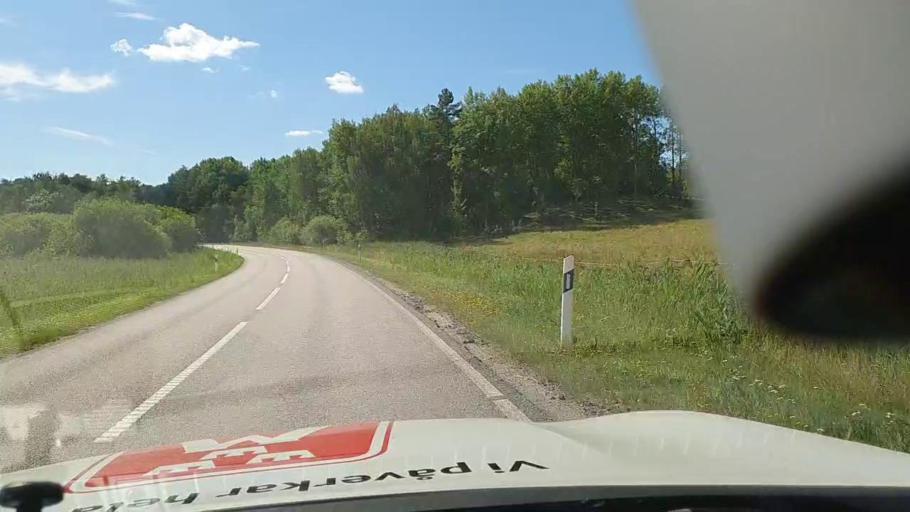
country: SE
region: Soedermanland
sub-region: Strangnas Kommun
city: Akers Styckebruk
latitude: 59.2577
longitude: 16.9417
